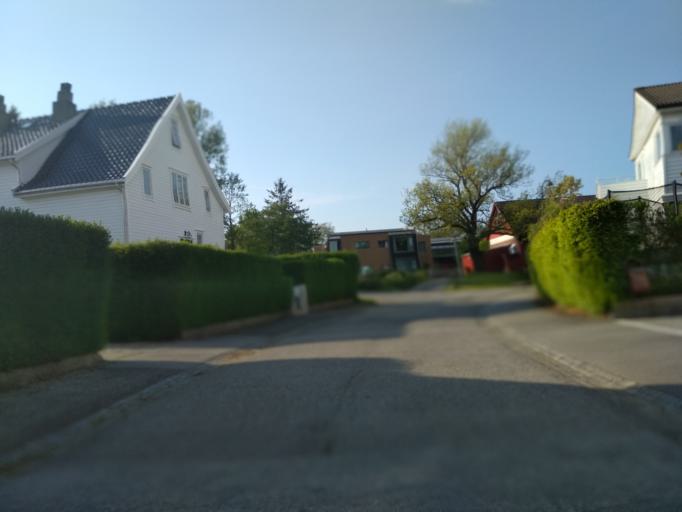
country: NO
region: Rogaland
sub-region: Stavanger
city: Stavanger
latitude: 58.9659
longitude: 5.7191
